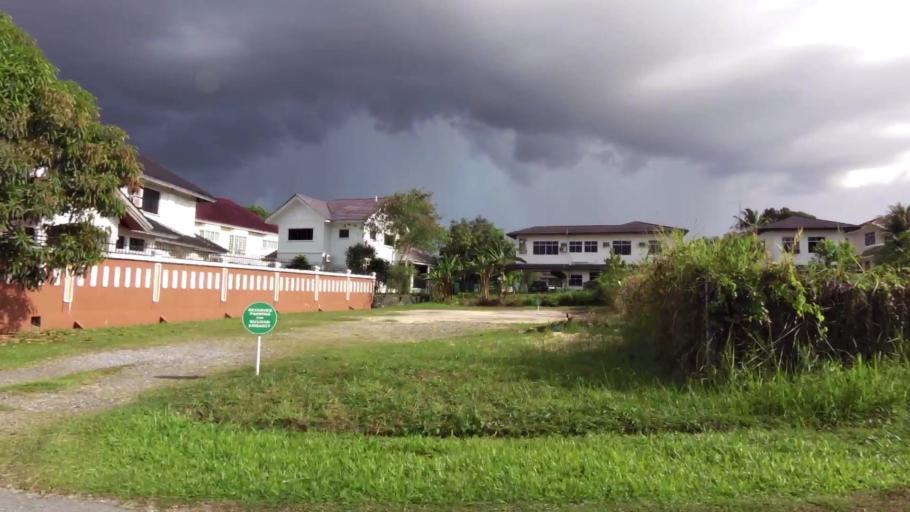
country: BN
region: Brunei and Muara
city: Bandar Seri Begawan
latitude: 4.9604
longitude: 114.9634
